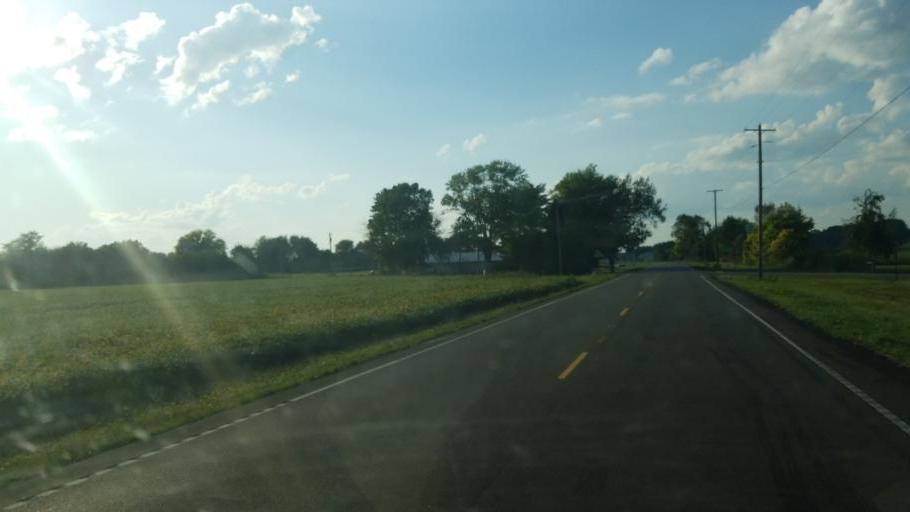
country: US
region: Ohio
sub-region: Knox County
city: Fredericktown
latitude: 40.4392
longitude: -82.5220
